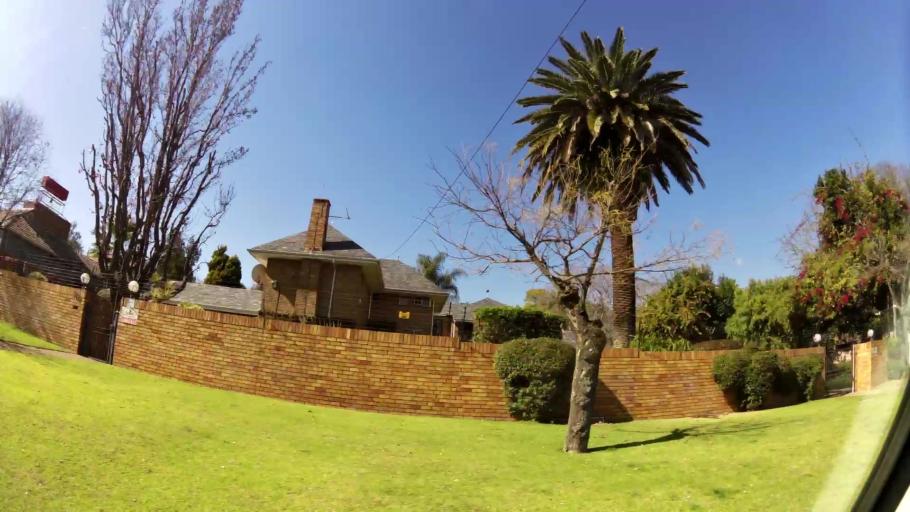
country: ZA
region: Gauteng
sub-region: City of Tshwane Metropolitan Municipality
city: Pretoria
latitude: -25.7710
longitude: 28.2375
